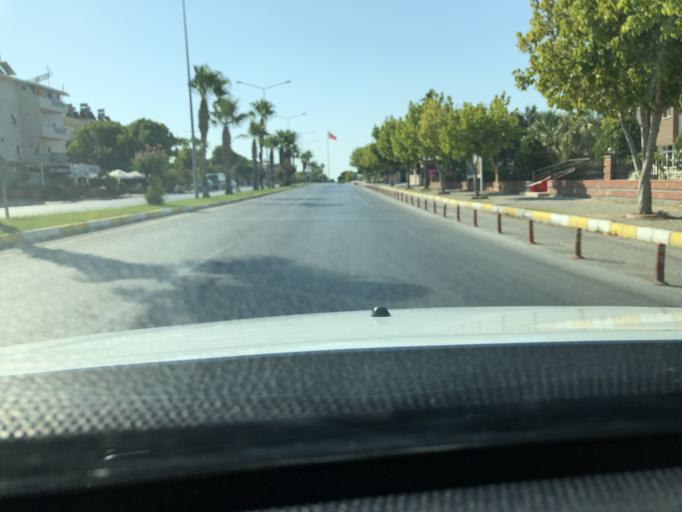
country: TR
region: Antalya
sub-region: Manavgat
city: Side
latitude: 36.7809
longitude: 31.3935
